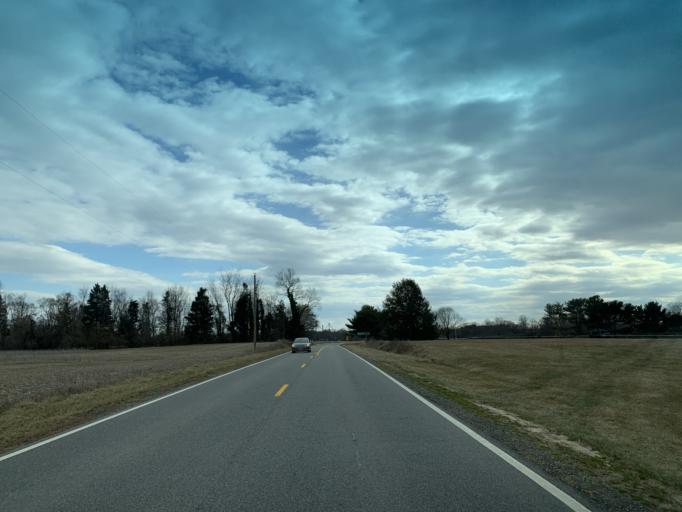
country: US
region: Maryland
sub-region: Queen Anne's County
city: Centreville
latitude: 38.9515
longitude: -76.0787
